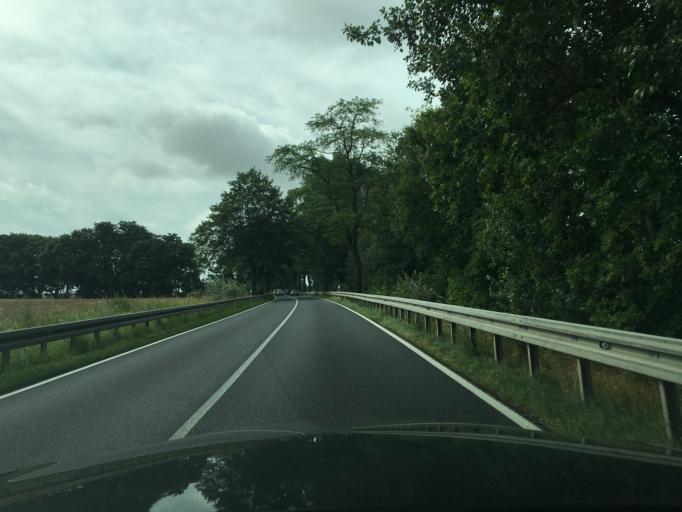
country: DE
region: Brandenburg
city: Gransee
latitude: 52.9633
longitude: 13.1490
